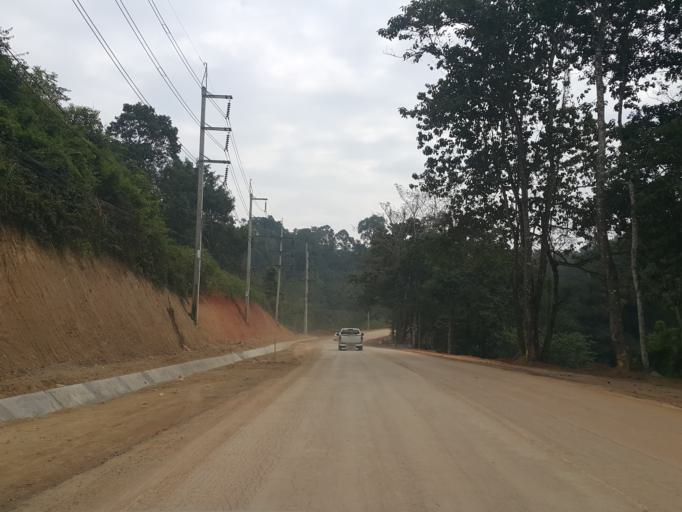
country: TH
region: Chiang Mai
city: Mae Taeng
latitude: 19.1428
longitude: 98.6978
